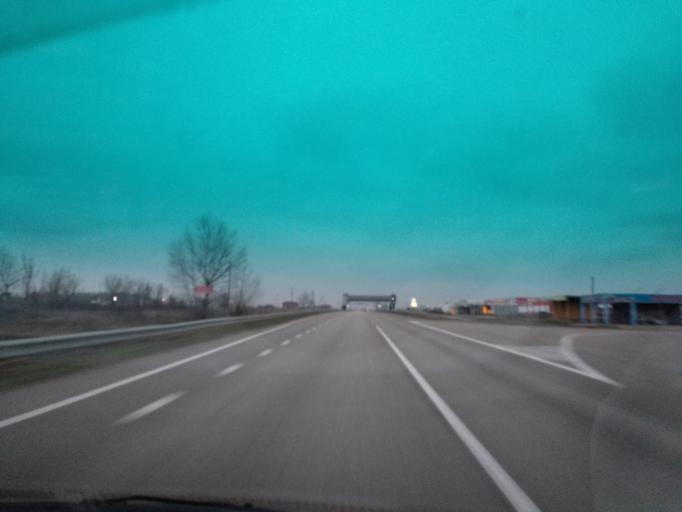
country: RU
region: Adygeya
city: Adygeysk
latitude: 44.8776
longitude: 39.1800
